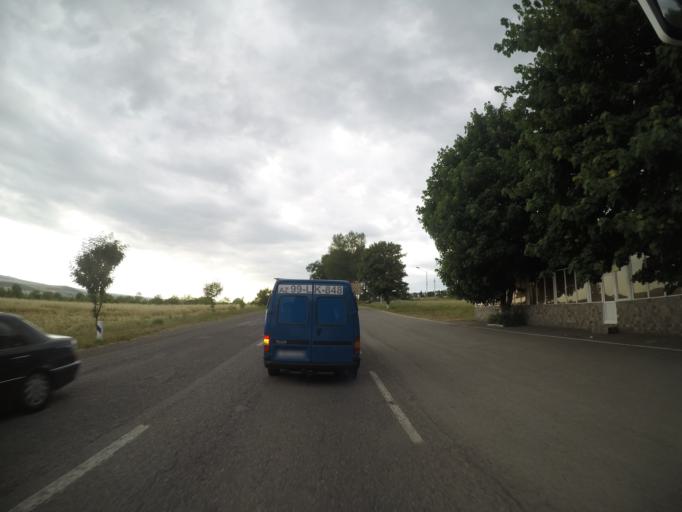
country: AZ
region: Ismayilli
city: Ismayilli
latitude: 40.7741
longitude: 48.2001
